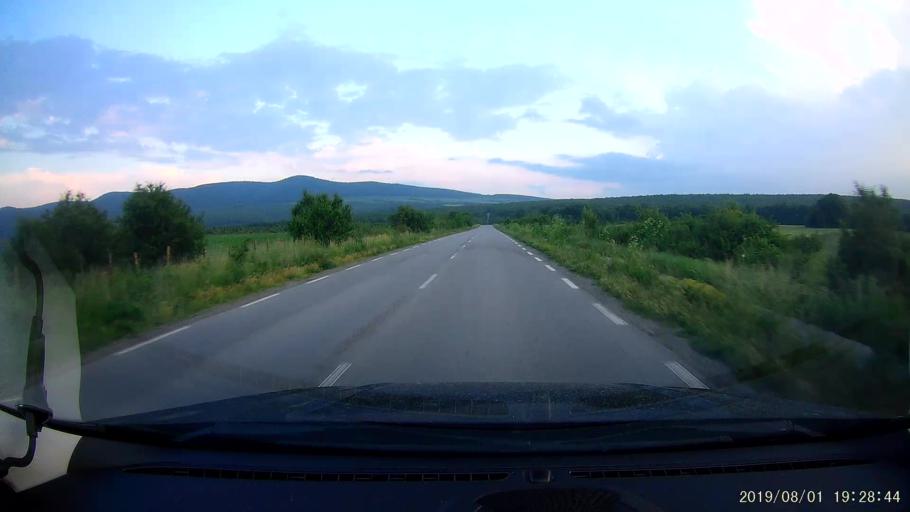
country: BG
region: Burgas
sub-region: Obshtina Sungurlare
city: Sungurlare
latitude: 42.8382
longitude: 26.9136
